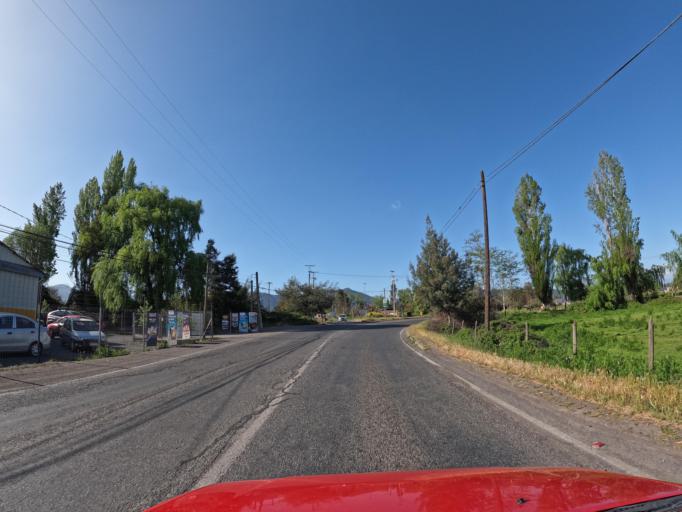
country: CL
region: Maule
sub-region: Provincia de Curico
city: Rauco
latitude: -34.8688
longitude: -71.2645
